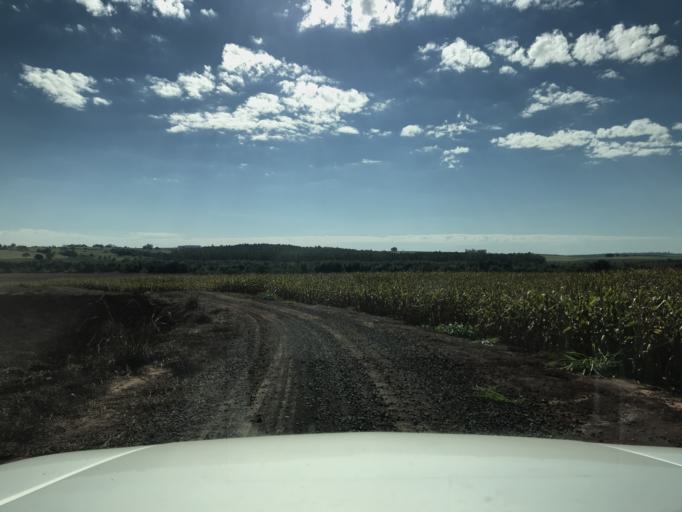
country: BR
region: Parana
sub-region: Palotina
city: Palotina
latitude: -24.1584
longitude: -53.7432
